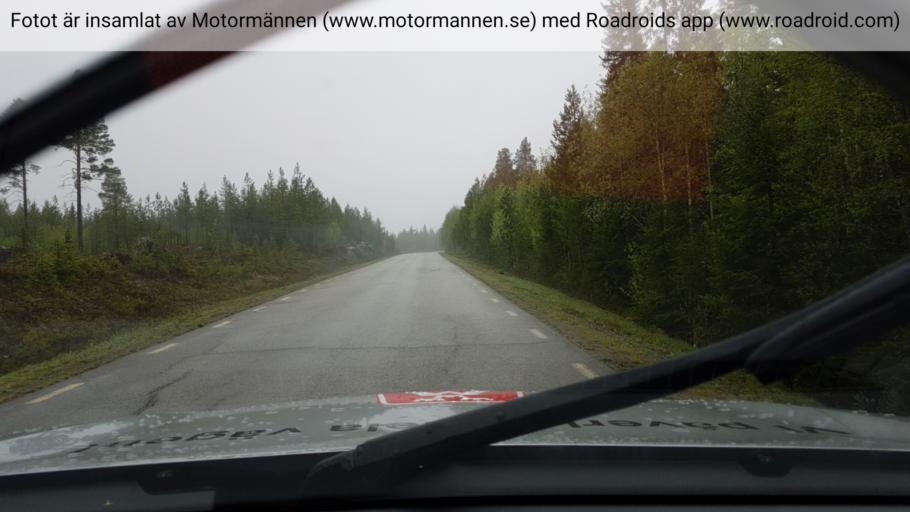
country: SE
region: Jaemtland
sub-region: Bergs Kommun
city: Hoverberg
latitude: 63.0295
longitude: 14.0584
